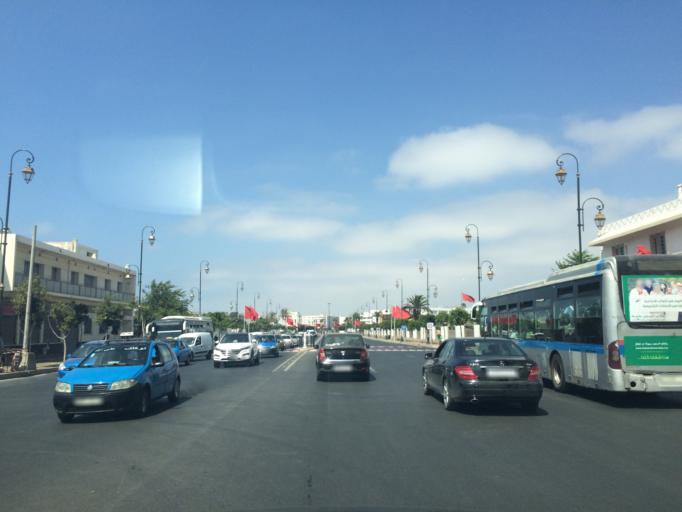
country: MA
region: Rabat-Sale-Zemmour-Zaer
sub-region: Rabat
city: Rabat
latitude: 34.0061
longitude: -6.8564
